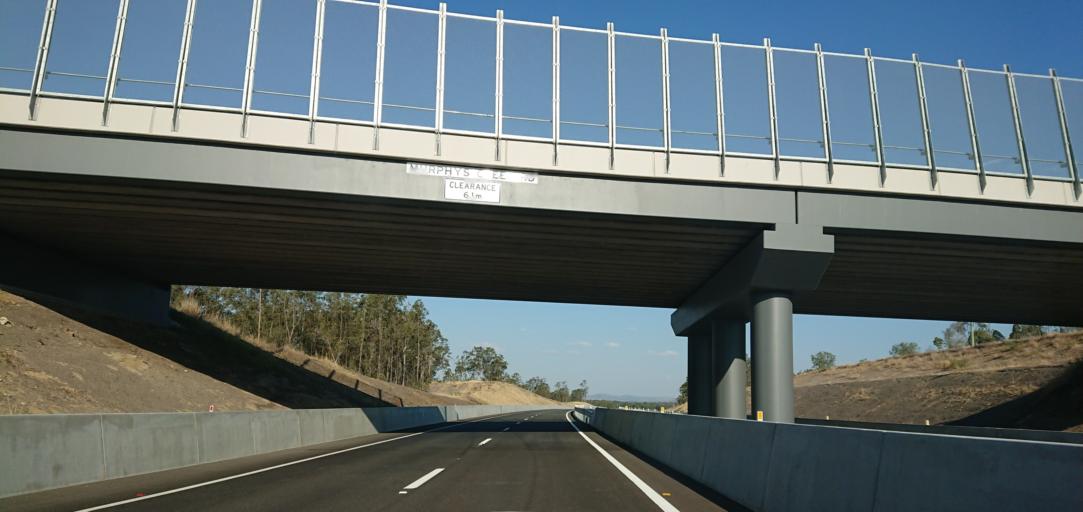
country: AU
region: Queensland
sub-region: Toowoomba
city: East Toowoomba
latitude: -27.5240
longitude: 152.0651
